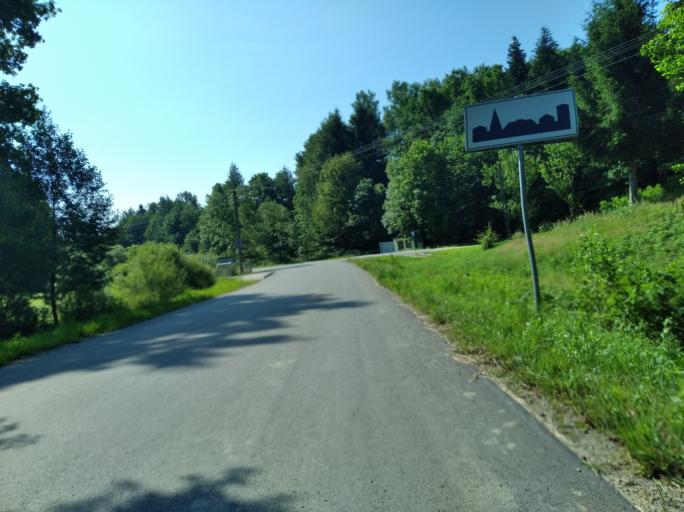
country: PL
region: Subcarpathian Voivodeship
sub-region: Powiat brzozowski
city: Wesola
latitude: 49.8288
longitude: 22.1503
